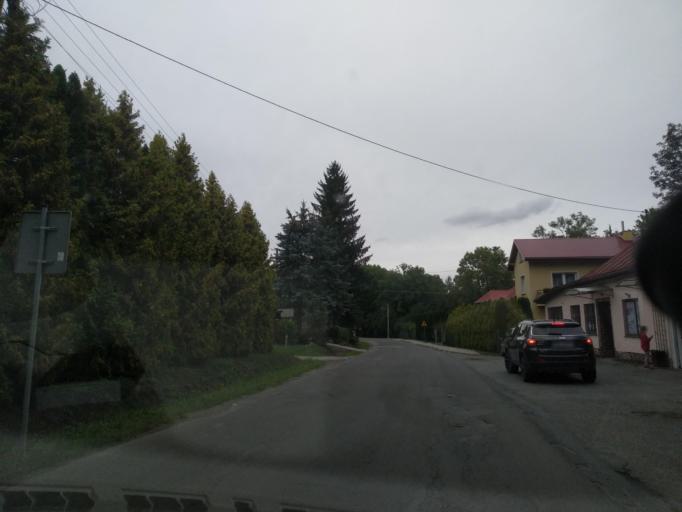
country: PL
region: Subcarpathian Voivodeship
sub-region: Powiat krosnienski
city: Iwonicz-Zdroj
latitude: 49.5782
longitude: 21.7526
